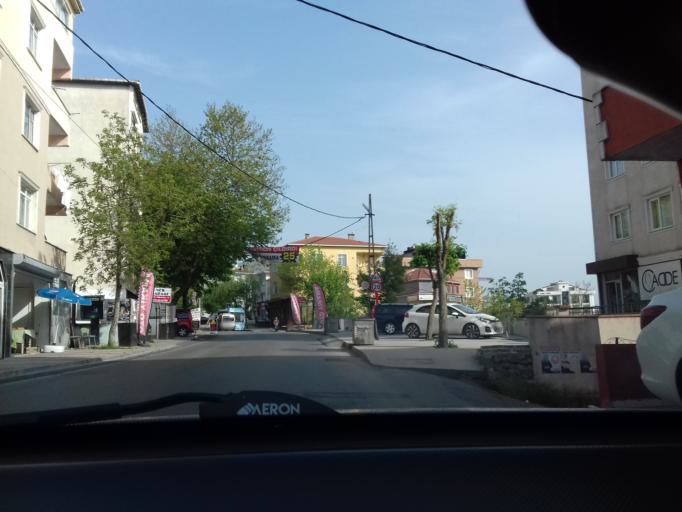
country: TR
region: Istanbul
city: Pendik
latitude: 40.9129
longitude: 29.2274
